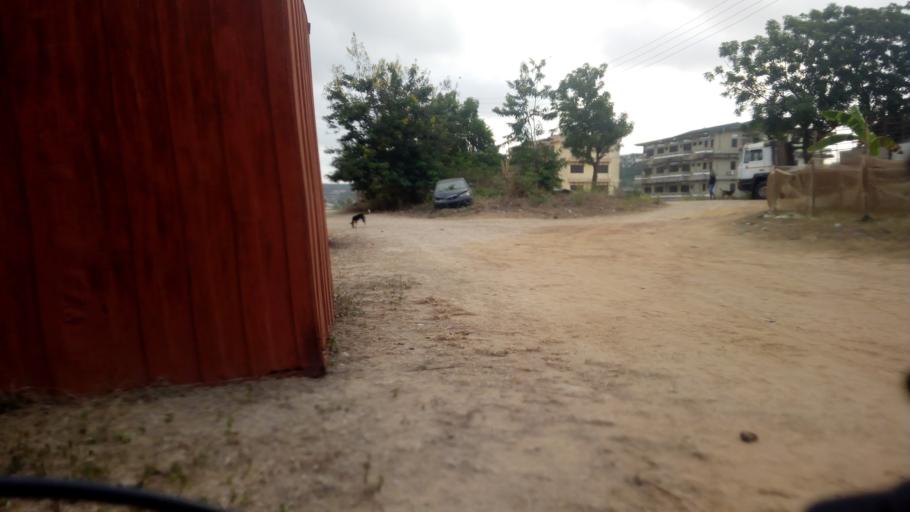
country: GH
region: Central
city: Cape Coast
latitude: 5.1205
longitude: -1.2697
